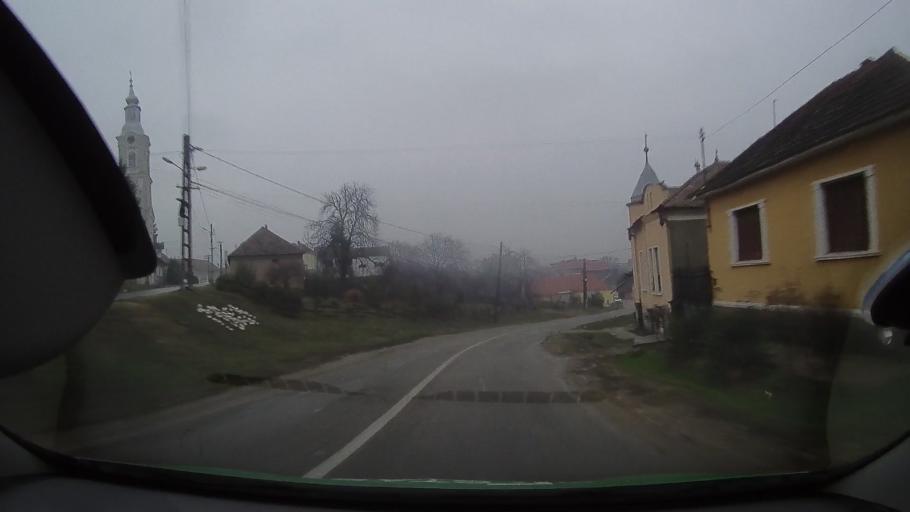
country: RO
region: Bihor
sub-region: Comuna Tinca
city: Tinca
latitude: 46.7732
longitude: 21.9282
